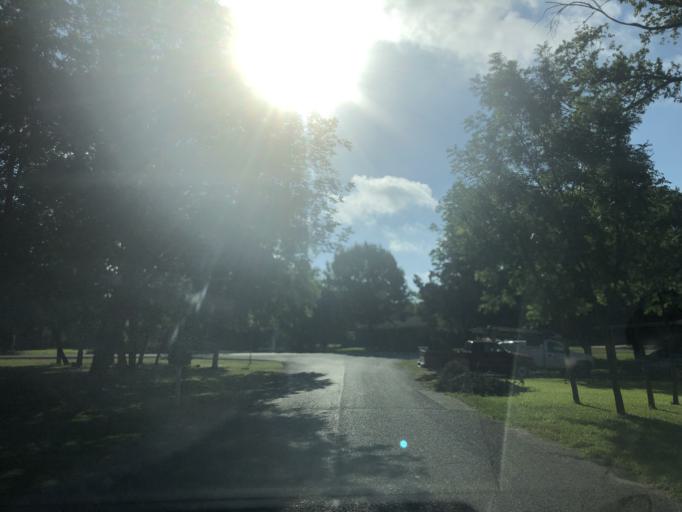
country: US
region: Texas
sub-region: Dallas County
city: Duncanville
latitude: 32.6639
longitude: -96.9191
